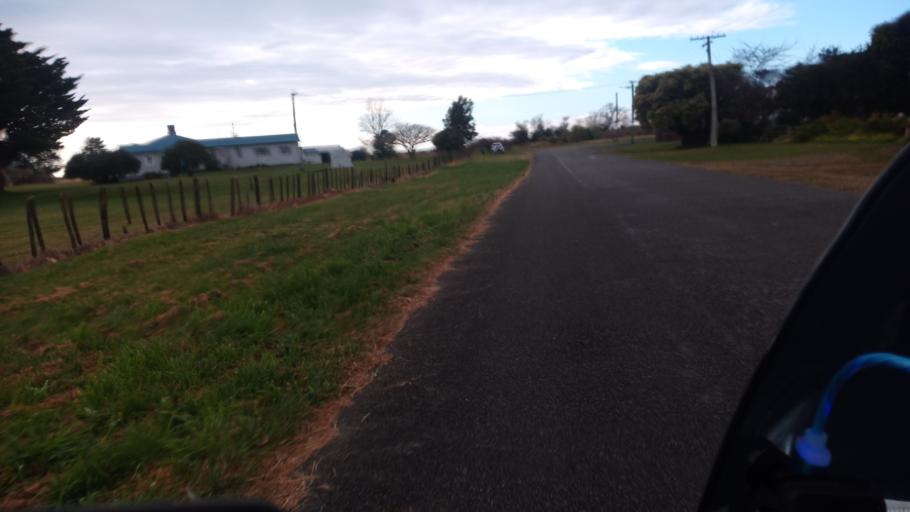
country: NZ
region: Gisborne
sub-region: Gisborne District
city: Gisborne
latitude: -38.3696
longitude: 178.3016
